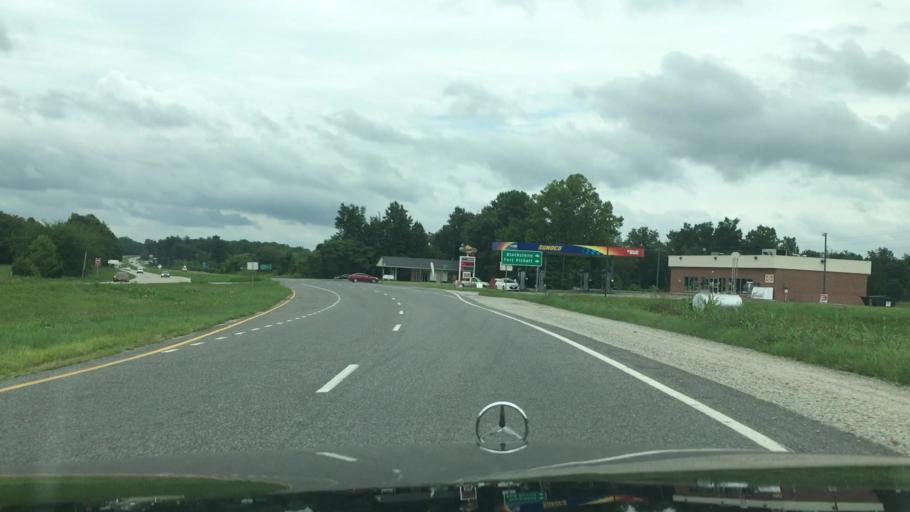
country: US
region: Virginia
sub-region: Amelia County
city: Amelia Court House
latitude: 37.3589
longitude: -77.8879
